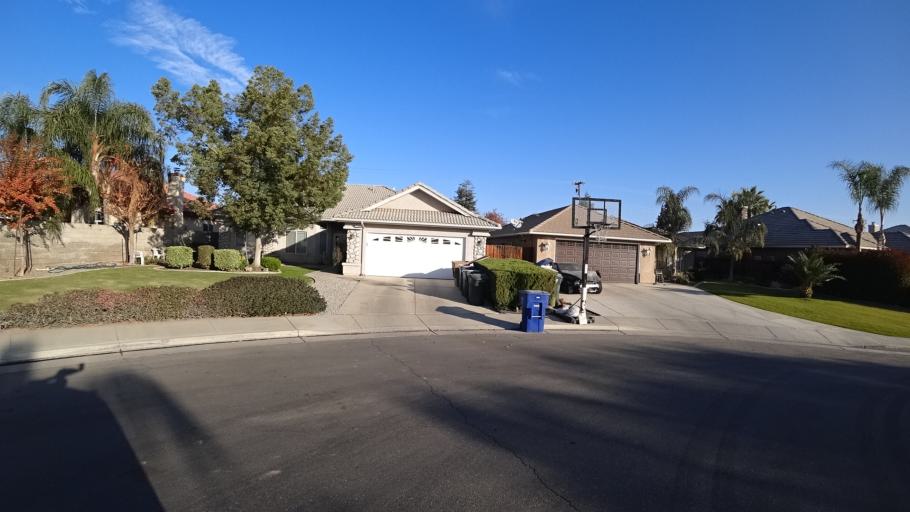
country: US
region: California
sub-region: Kern County
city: Greenfield
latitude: 35.2736
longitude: -119.0511
